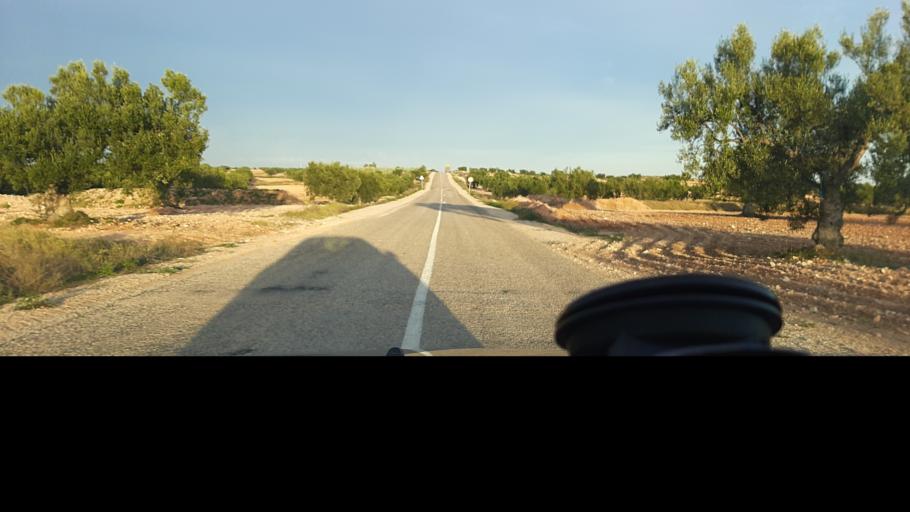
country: TN
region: Safaqis
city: Sfax
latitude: 34.9533
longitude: 10.5516
